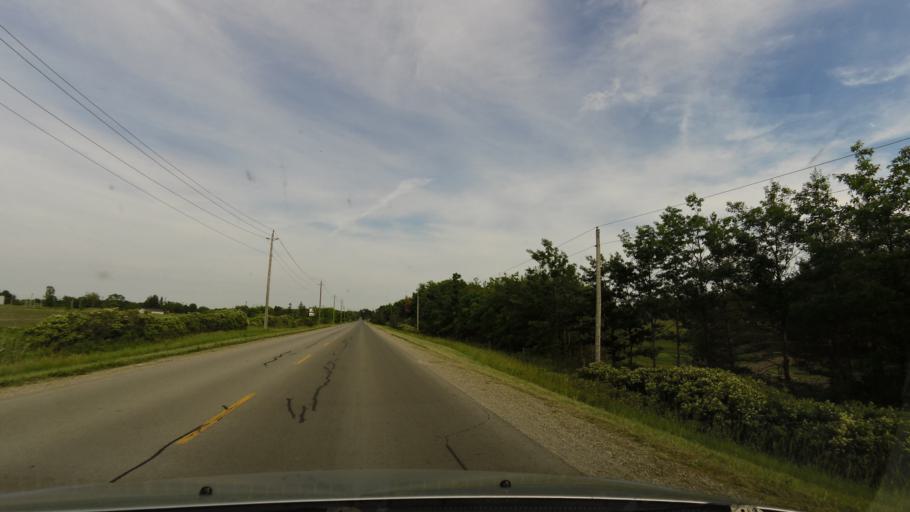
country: CA
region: Ontario
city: Ancaster
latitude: 43.0264
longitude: -80.0030
